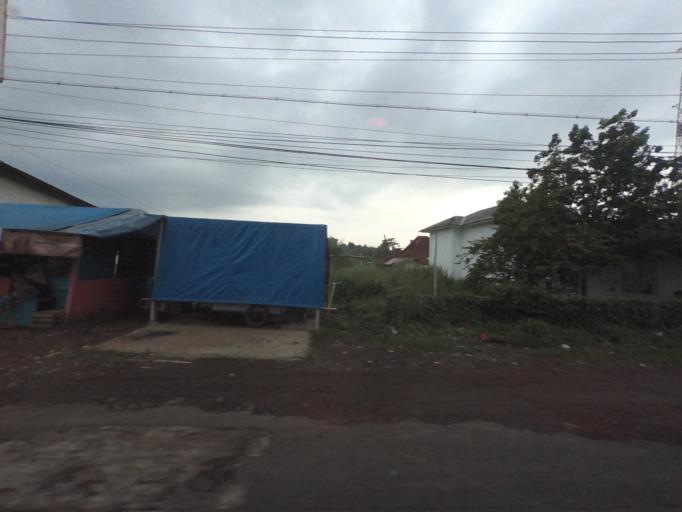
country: ID
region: West Java
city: Cicurug
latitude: -6.8438
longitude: 106.7615
